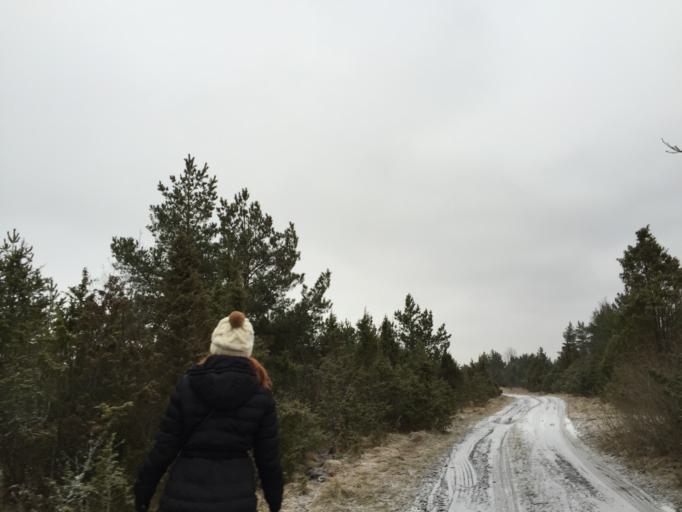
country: EE
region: Saare
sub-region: Orissaare vald
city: Orissaare
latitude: 58.6062
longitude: 23.1147
